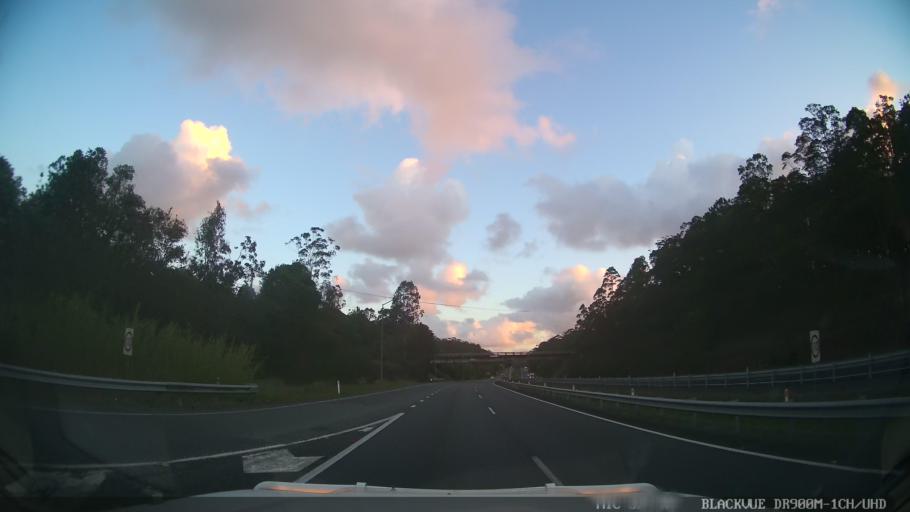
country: AU
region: Queensland
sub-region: Sunshine Coast
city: Twin Waters
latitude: -26.5934
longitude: 152.9706
